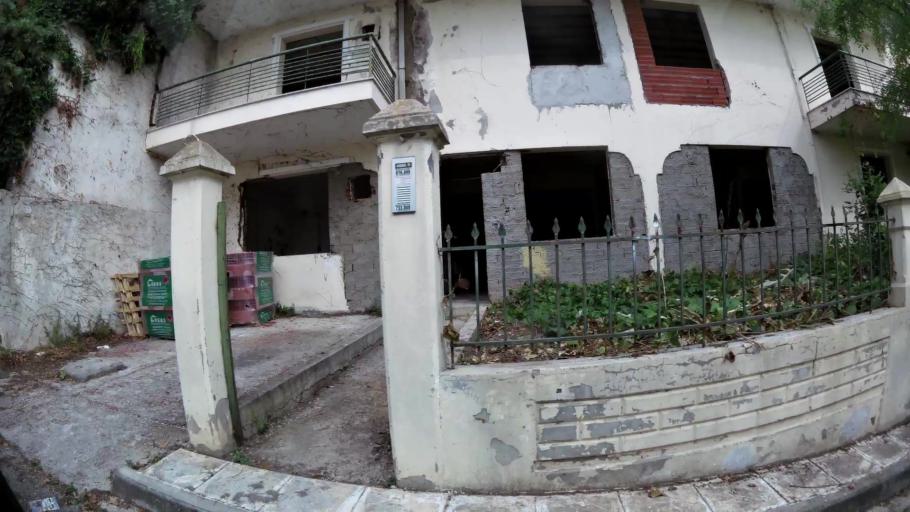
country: GR
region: Central Macedonia
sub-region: Nomos Thessalonikis
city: Oraiokastro
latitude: 40.7124
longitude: 22.9235
